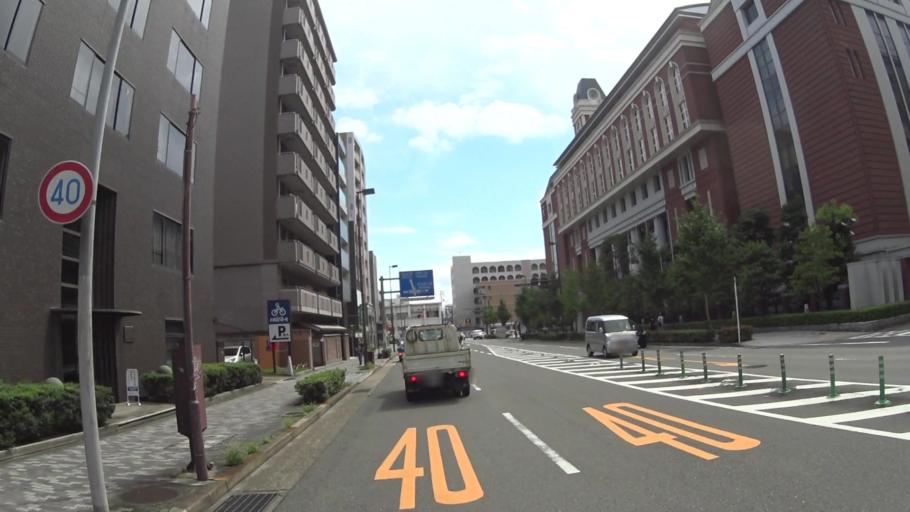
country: JP
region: Kyoto
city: Kyoto
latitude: 35.0100
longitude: 135.7427
